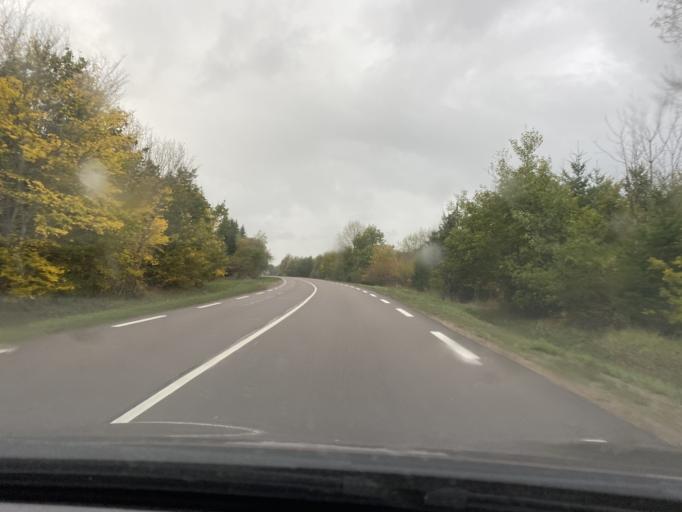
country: FR
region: Bourgogne
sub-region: Departement de la Cote-d'Or
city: Saulieu
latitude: 47.3089
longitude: 4.2069
